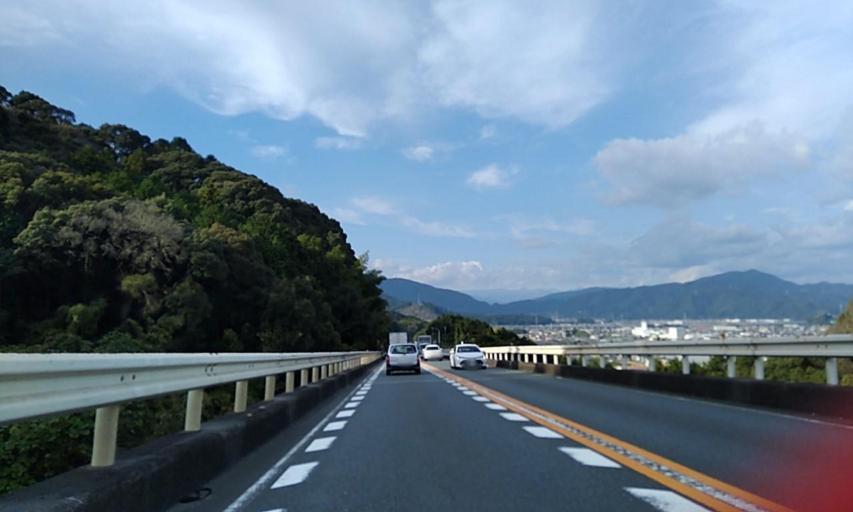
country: JP
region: Shizuoka
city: Kanaya
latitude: 34.8270
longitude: 138.1206
